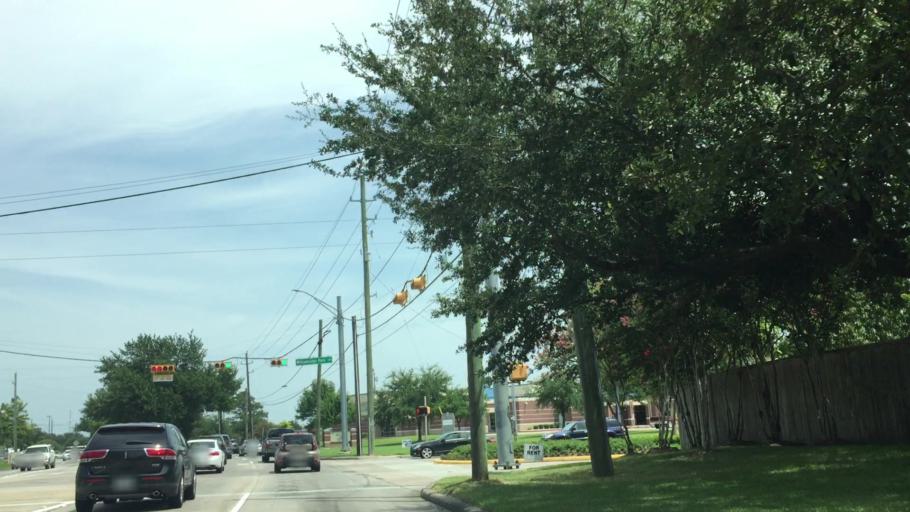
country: US
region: Texas
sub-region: Harris County
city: Jersey Village
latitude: 29.9038
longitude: -95.5582
